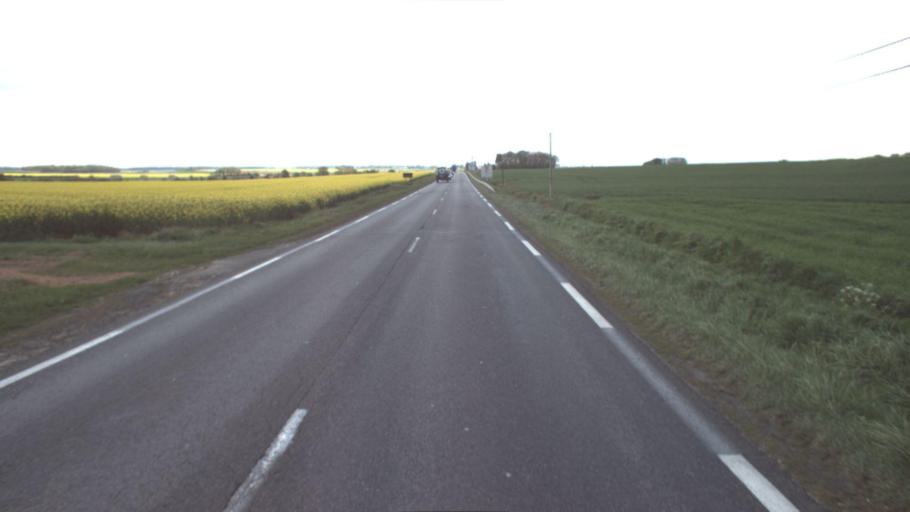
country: FR
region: Ile-de-France
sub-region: Departement de Seine-et-Marne
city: Jouy-le-Chatel
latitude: 48.6877
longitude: 3.1191
